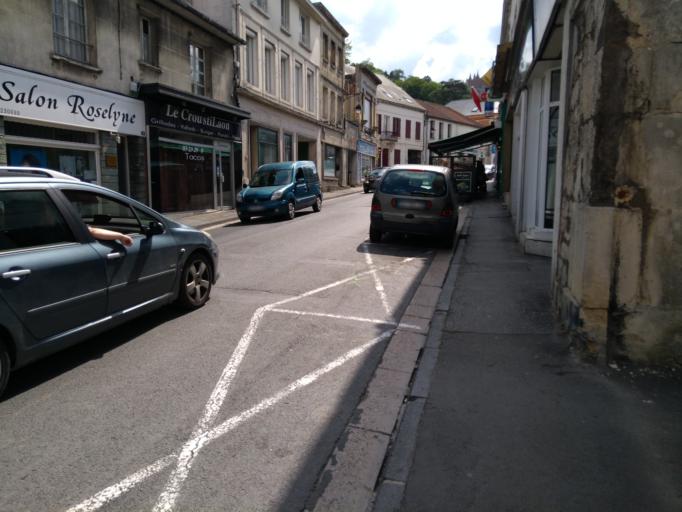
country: FR
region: Picardie
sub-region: Departement de l'Aisne
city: Laon
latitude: 49.5685
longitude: 3.6316
